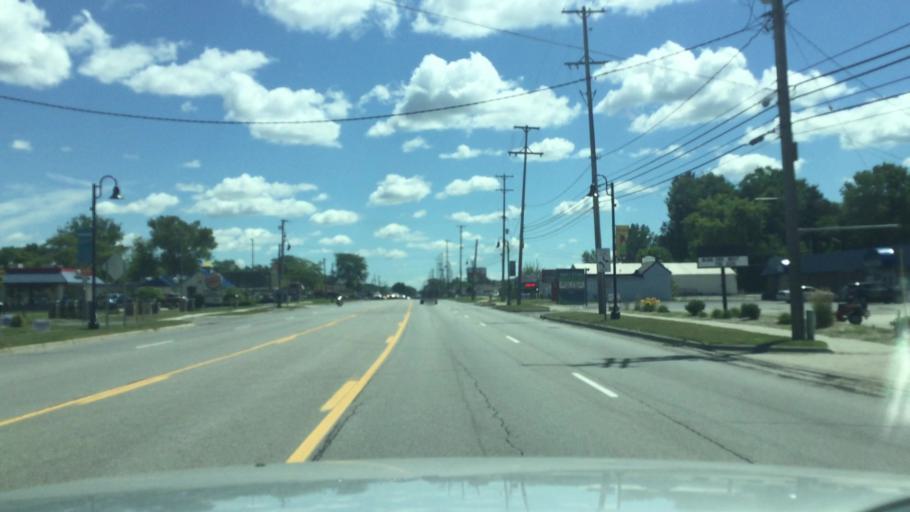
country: US
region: Michigan
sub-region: Saginaw County
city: Shields
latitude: 43.4159
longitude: -84.0701
